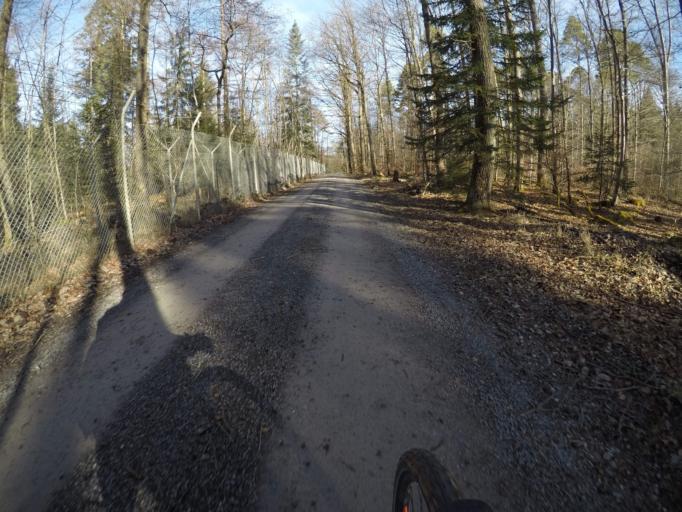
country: DE
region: Baden-Wuerttemberg
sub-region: Regierungsbezirk Stuttgart
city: Steinenbronn
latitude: 48.6898
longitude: 9.0874
